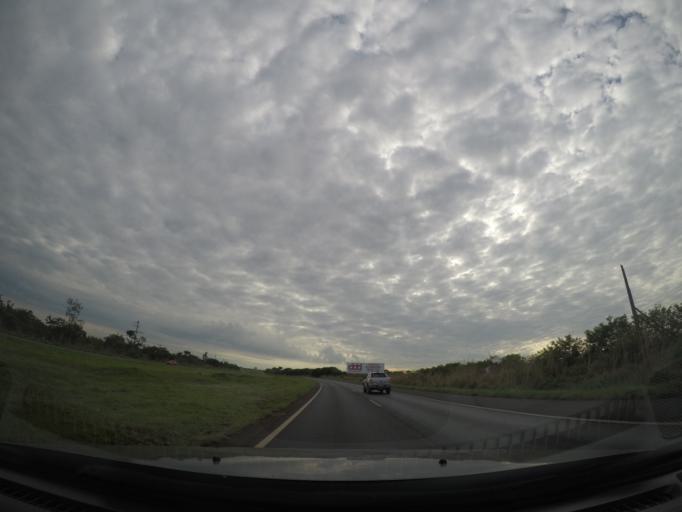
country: BR
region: Goias
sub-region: Planaltina
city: Planaltina
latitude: -15.5987
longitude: -47.6168
